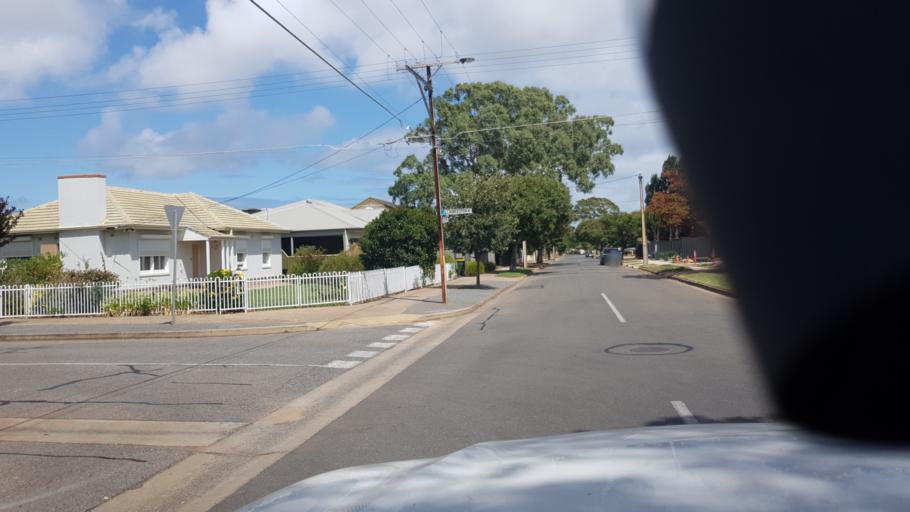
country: AU
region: South Australia
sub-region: Adelaide
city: Brighton
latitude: -35.0168
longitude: 138.5350
